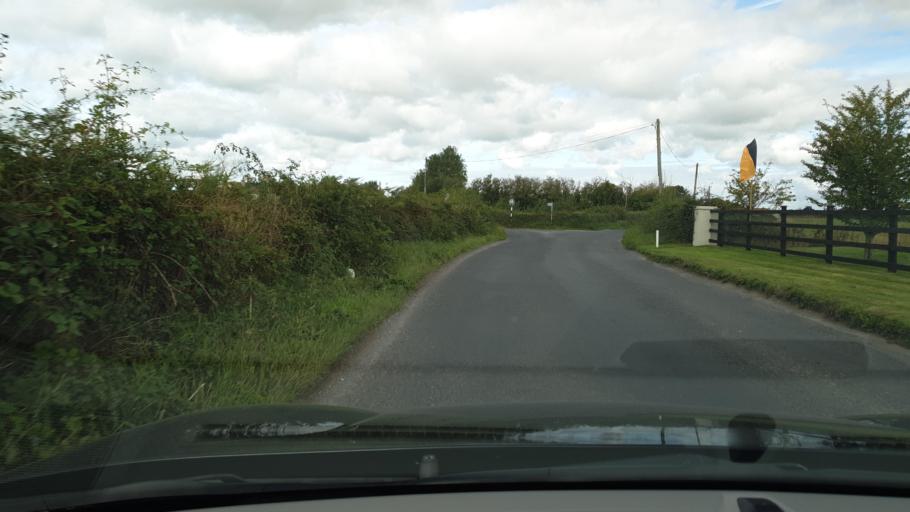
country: IE
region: Leinster
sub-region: Laois
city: Portlaoise
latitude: 53.0633
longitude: -7.2621
